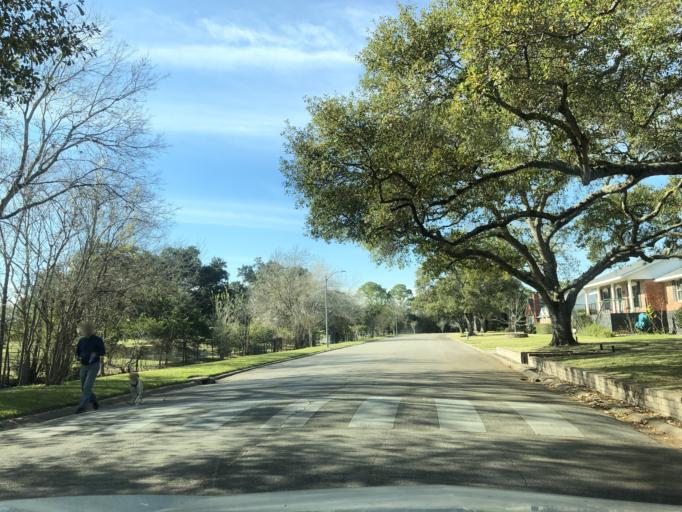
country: US
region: Texas
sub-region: Fort Bend County
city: Missouri City
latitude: 29.6772
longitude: -95.5159
